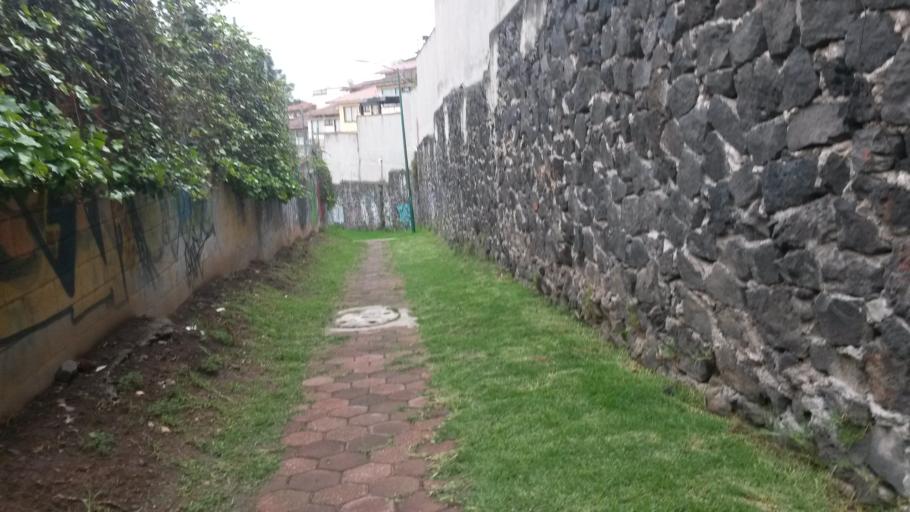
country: MX
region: Mexico City
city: Magdalena Contreras
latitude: 19.3008
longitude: -99.2391
